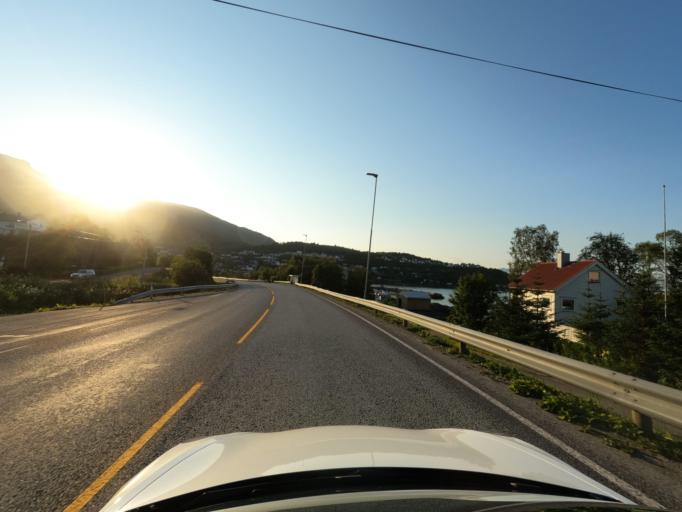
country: NO
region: Troms
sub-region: Harstad
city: Harstad
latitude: 68.7437
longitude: 16.5670
